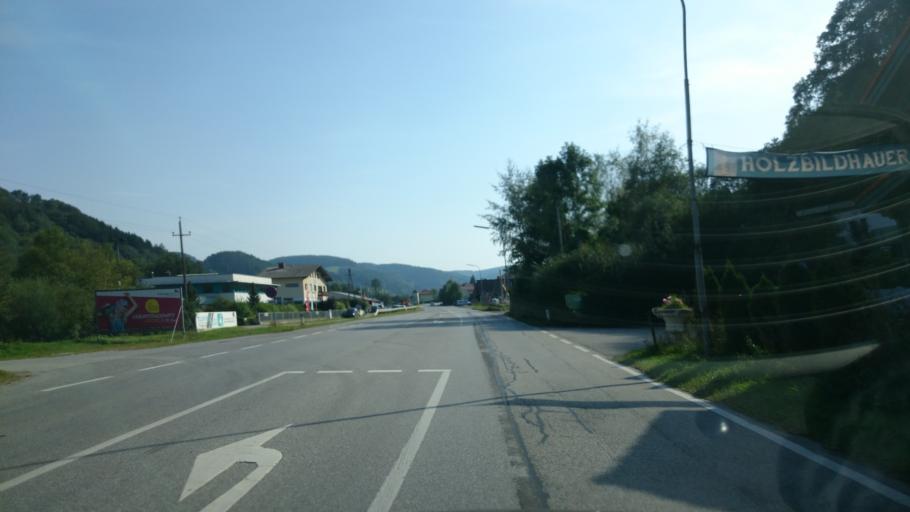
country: AT
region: Lower Austria
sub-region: Politischer Bezirk Neunkirchen
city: Edlitz
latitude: 47.5827
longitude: 16.0998
